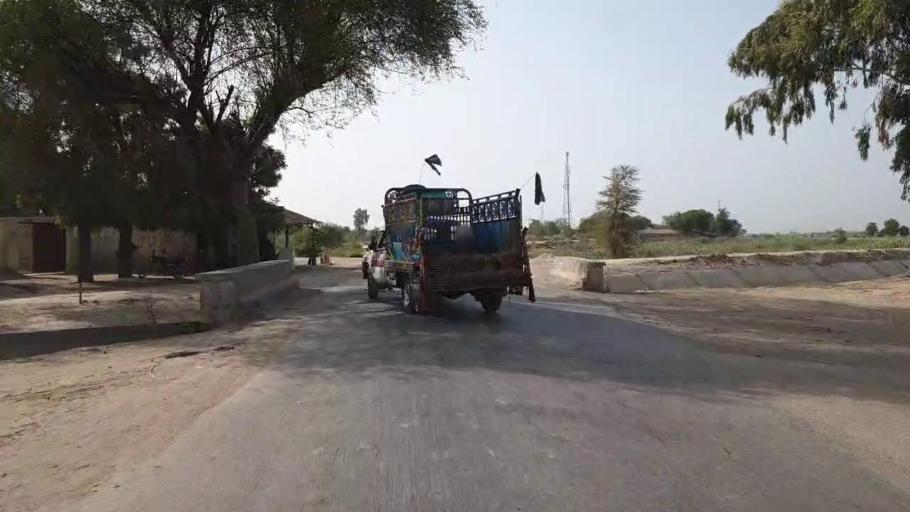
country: PK
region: Sindh
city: Sanghar
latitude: 26.2640
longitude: 68.9298
